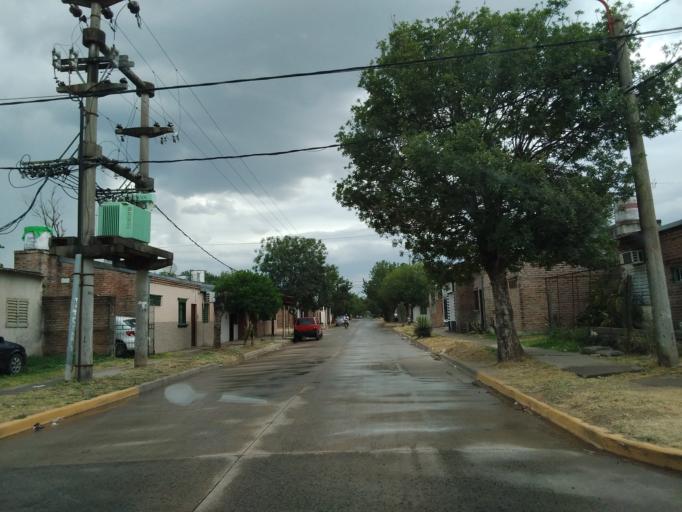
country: AR
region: Corrientes
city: Corrientes
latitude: -27.5188
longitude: -58.7892
